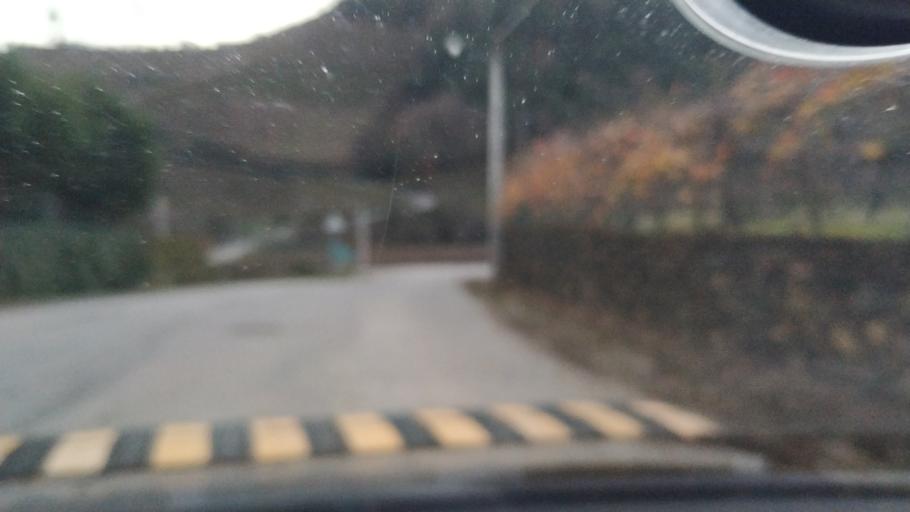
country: PT
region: Vila Real
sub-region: Santa Marta de Penaguiao
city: Santa Marta de Penaguiao
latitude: 41.2339
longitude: -7.7791
